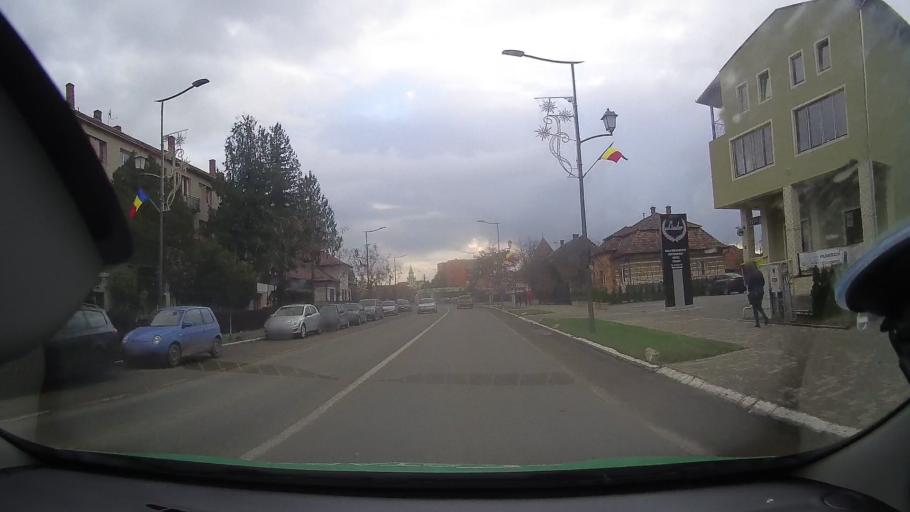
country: RO
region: Cluj
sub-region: Municipiul Campia Turzii
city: Campia Turzii
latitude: 46.5408
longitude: 23.8900
